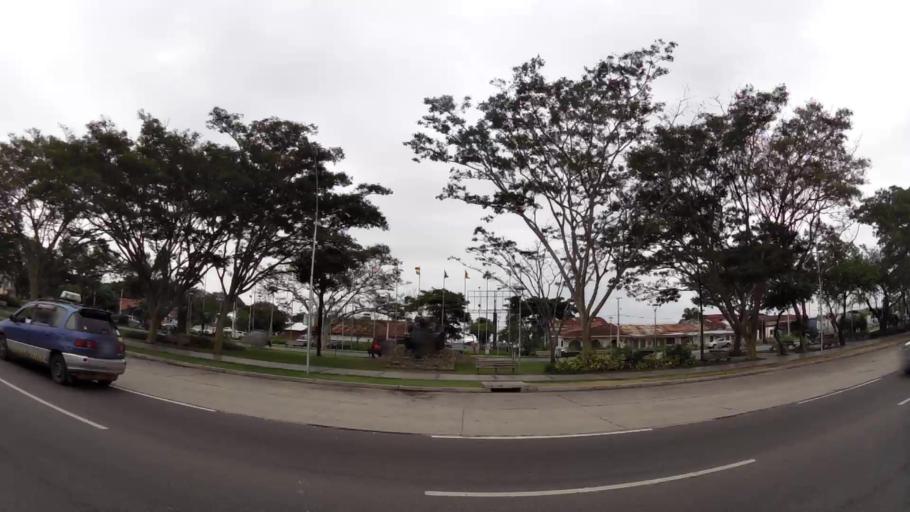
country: BO
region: Santa Cruz
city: Santa Cruz de la Sierra
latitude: -17.7987
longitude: -63.1775
